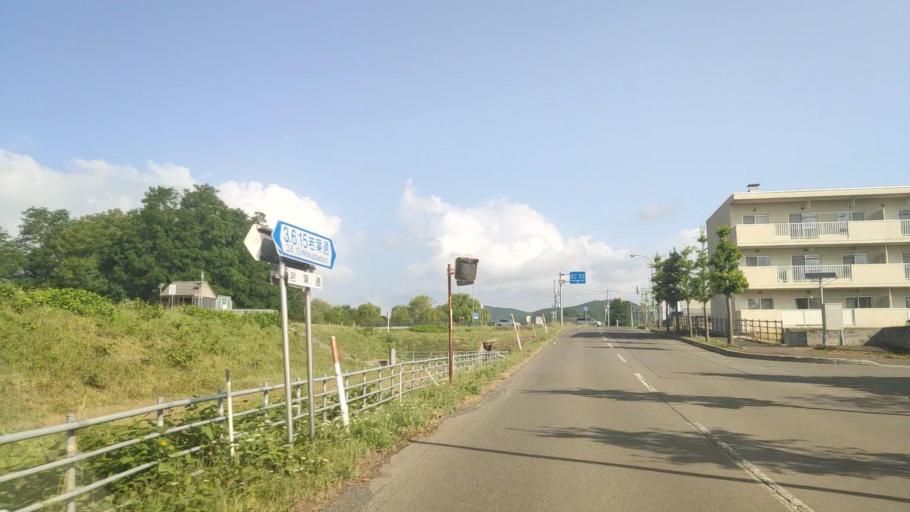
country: JP
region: Hokkaido
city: Shimo-furano
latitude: 43.3441
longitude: 142.3766
